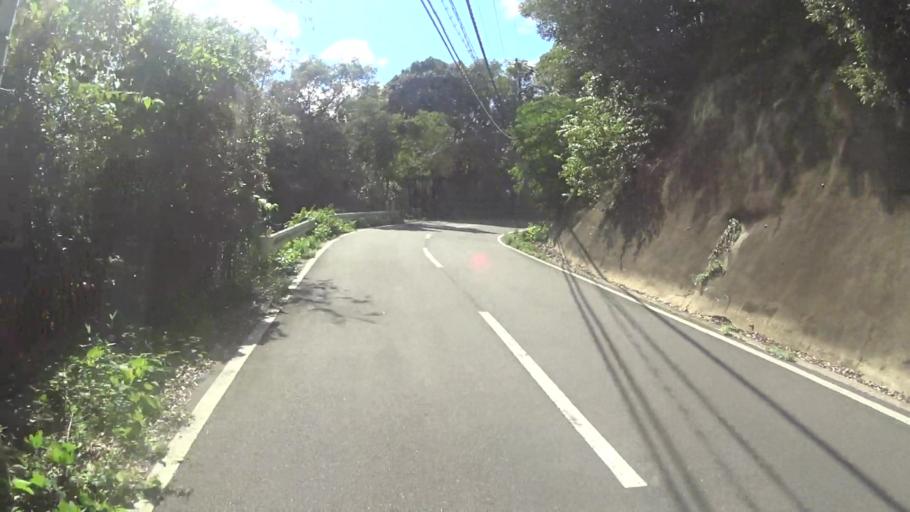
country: JP
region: Mie
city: Ueno-ebisumachi
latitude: 34.7428
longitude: 136.0089
